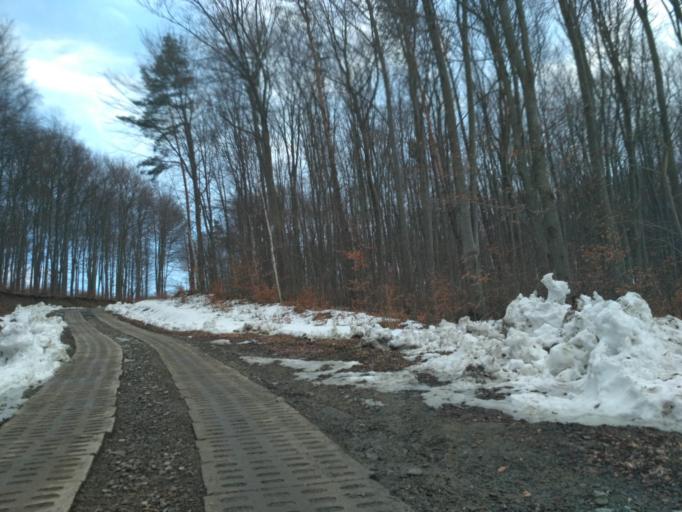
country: PL
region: Subcarpathian Voivodeship
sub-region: Powiat brzozowski
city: Dydnia
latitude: 49.6420
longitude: 22.1951
